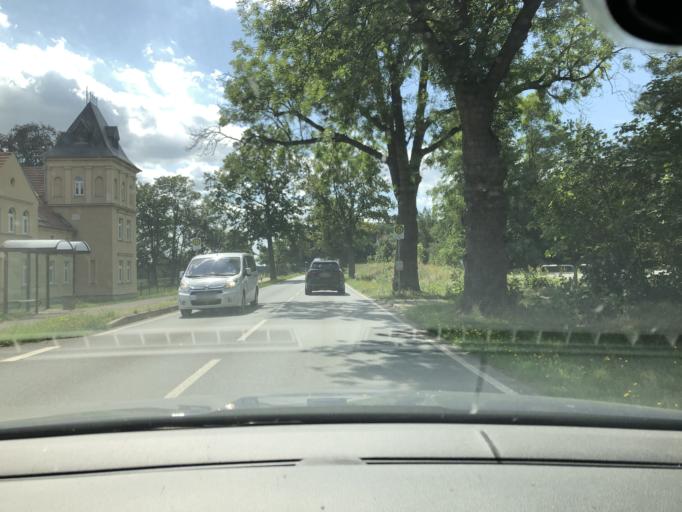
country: DE
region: Brandenburg
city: Wittstock
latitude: 53.1341
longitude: 12.4891
